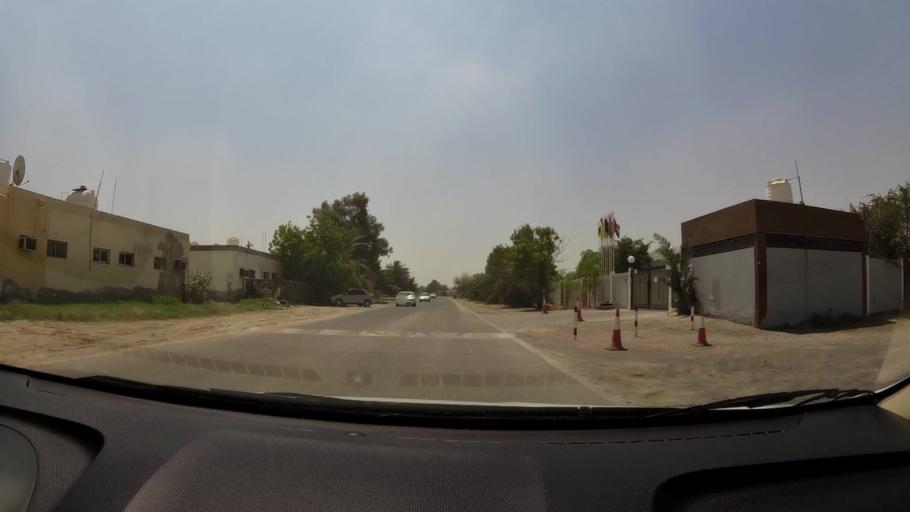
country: AE
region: Umm al Qaywayn
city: Umm al Qaywayn
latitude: 25.5579
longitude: 55.5542
